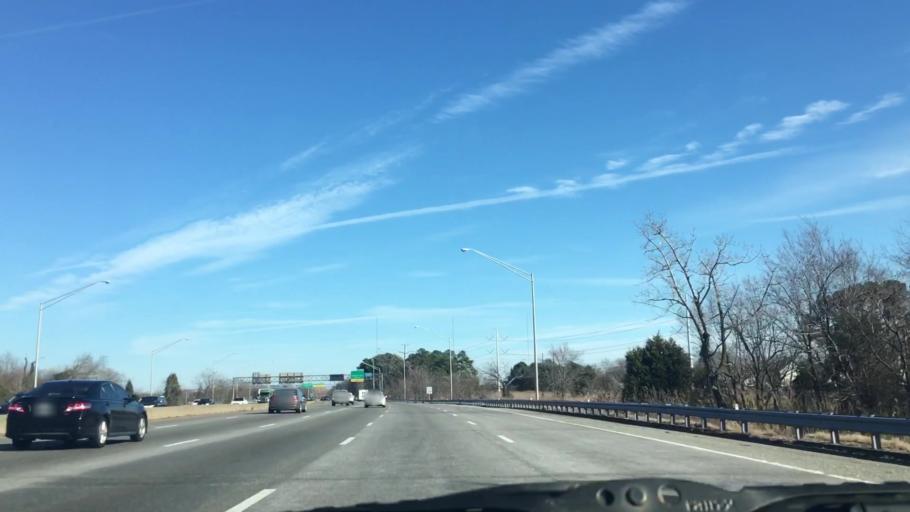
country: US
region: Virginia
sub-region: City of Hampton
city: Hampton
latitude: 37.0329
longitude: -76.3742
